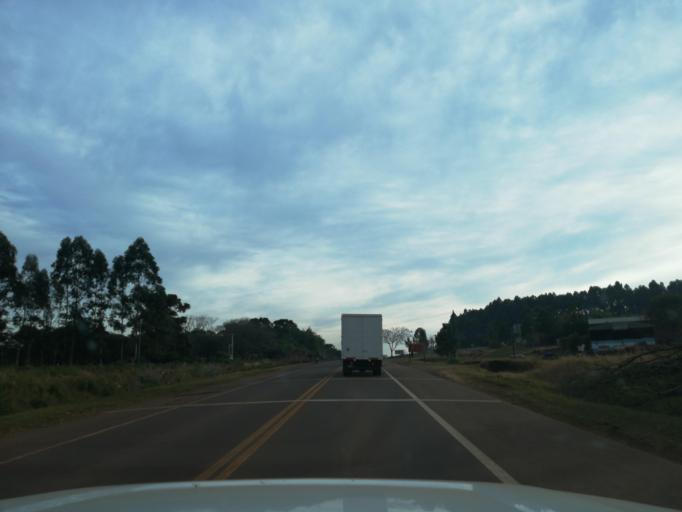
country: AR
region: Misiones
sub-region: Departamento de San Pedro
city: San Pedro
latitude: -26.6266
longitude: -54.1223
